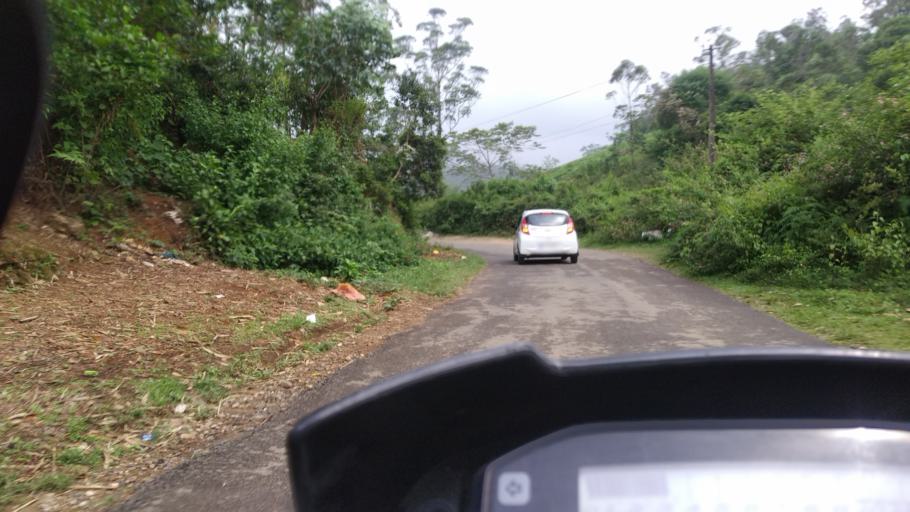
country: IN
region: Kerala
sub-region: Kottayam
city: Erattupetta
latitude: 9.5866
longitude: 77.0092
